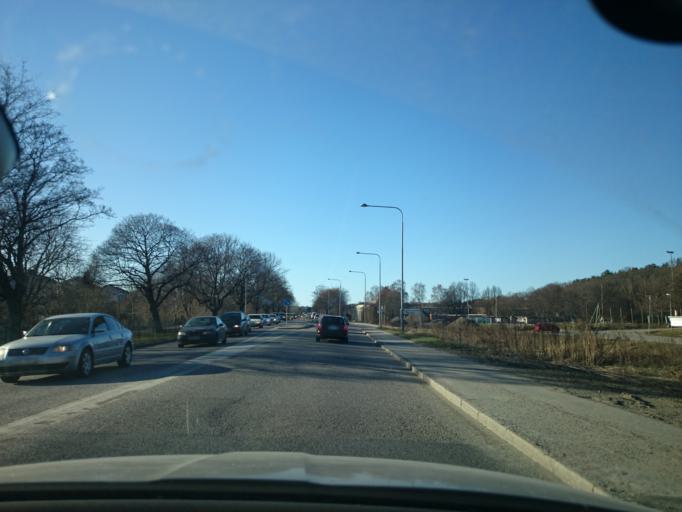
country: SE
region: Stockholm
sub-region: Huddinge Kommun
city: Huddinge
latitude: 59.2813
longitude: 17.9993
